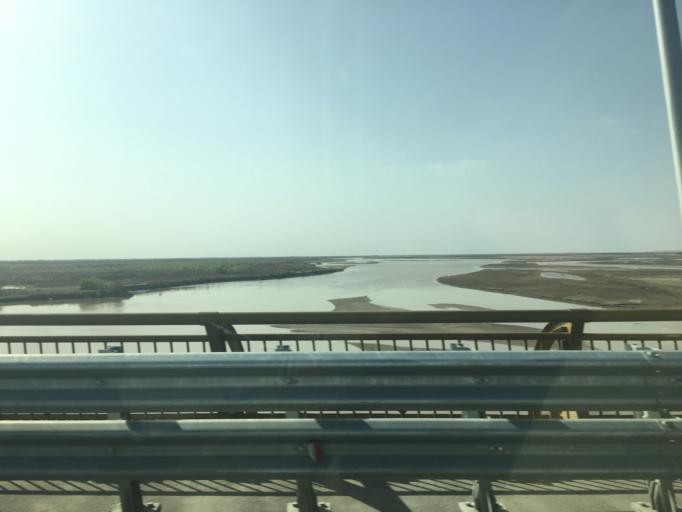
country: TM
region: Lebap
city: Turkmenabat
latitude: 39.1303
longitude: 63.5684
